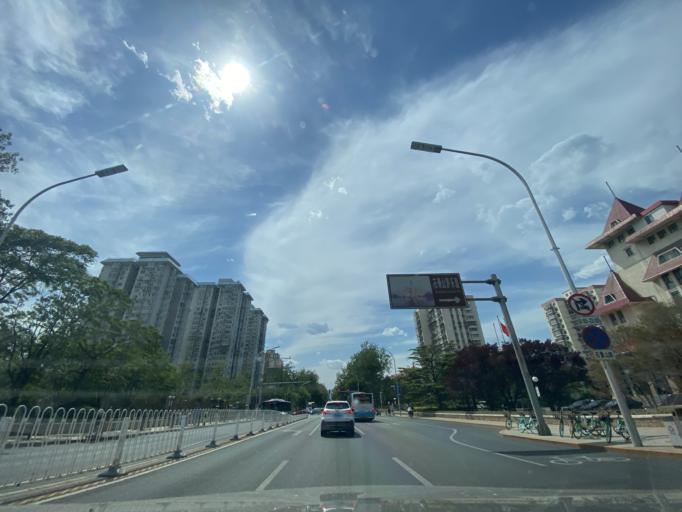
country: CN
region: Beijing
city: Lugu
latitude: 39.9062
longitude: 116.1939
